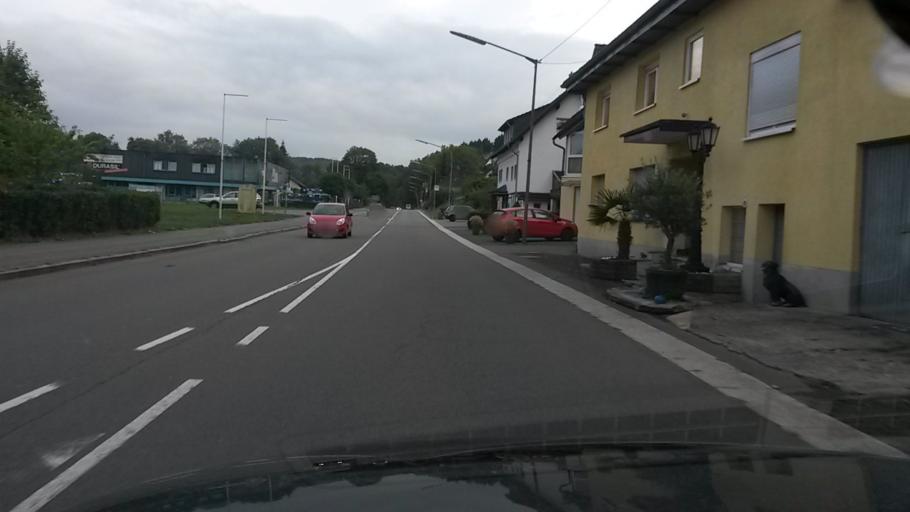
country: DE
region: North Rhine-Westphalia
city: Wiehl
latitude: 50.9703
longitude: 7.4859
